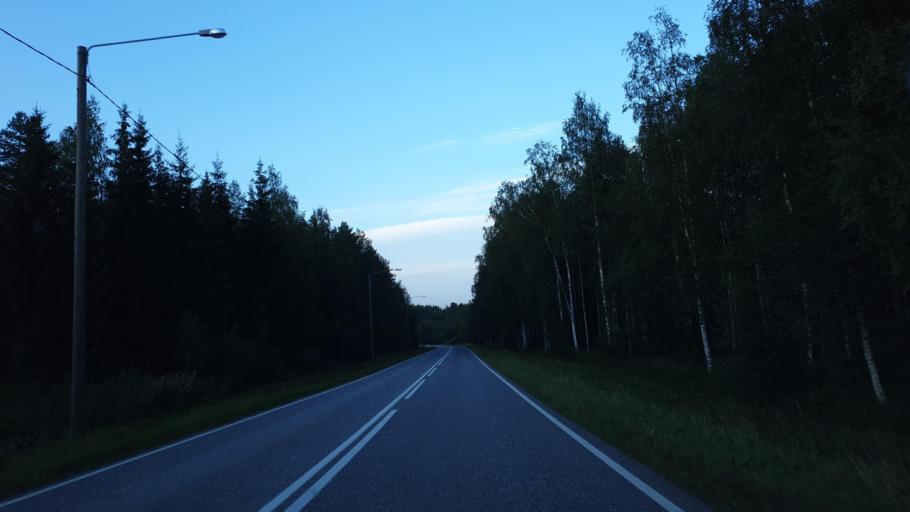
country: FI
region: Northern Savo
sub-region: Koillis-Savo
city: Kaavi
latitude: 62.9730
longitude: 28.7749
